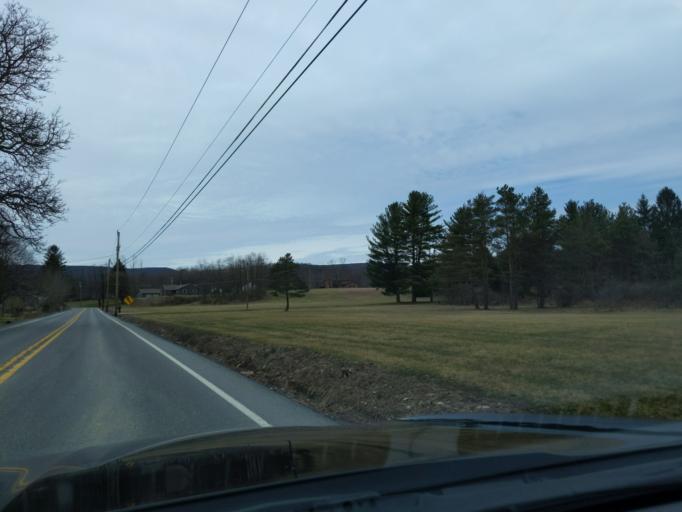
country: US
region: Pennsylvania
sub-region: Blair County
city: Greenwood
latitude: 40.5583
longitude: -78.3794
